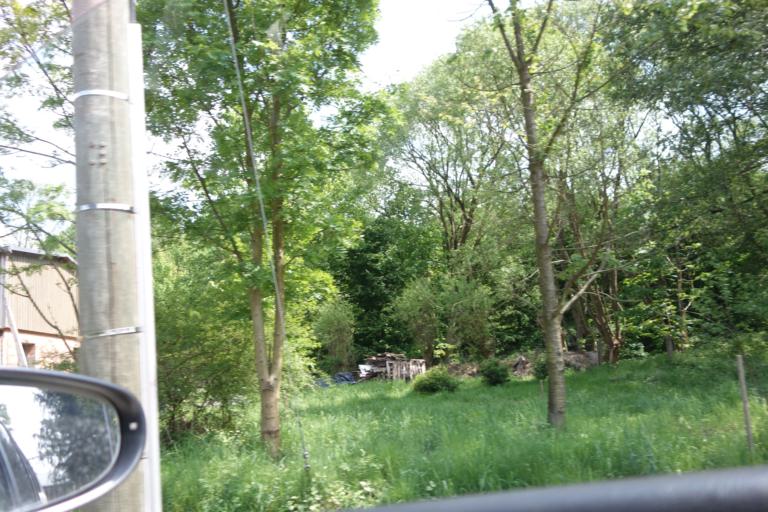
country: DE
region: Saxony
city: Eppendorf
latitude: 50.8148
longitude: 13.2560
